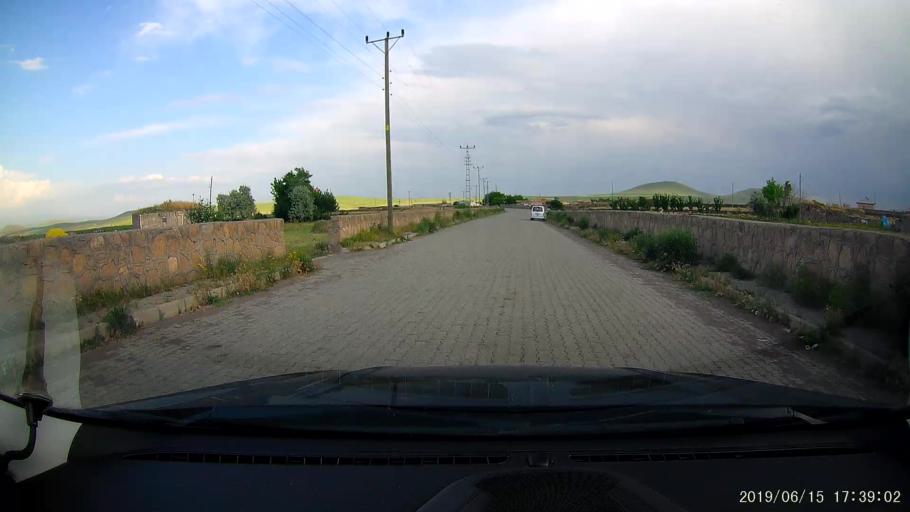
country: TR
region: Kars
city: Basgedikler
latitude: 40.5181
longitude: 43.5689
